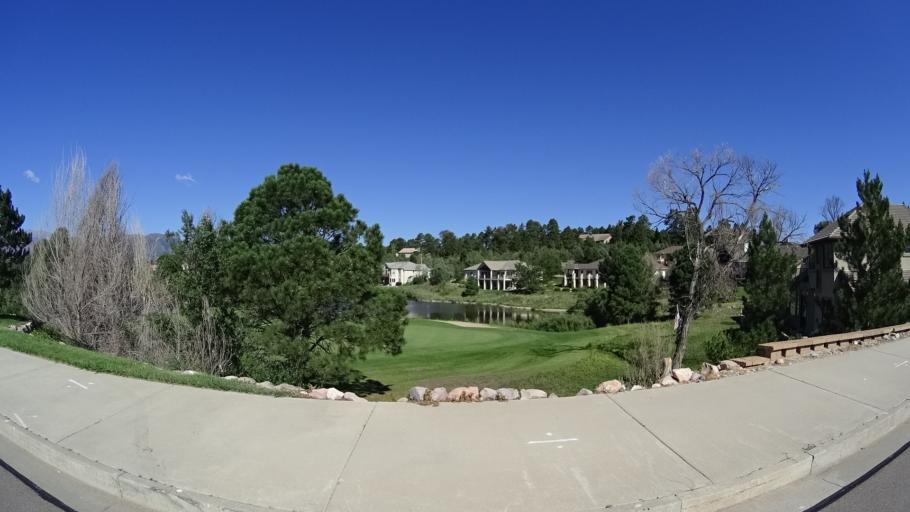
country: US
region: Colorado
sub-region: El Paso County
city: Air Force Academy
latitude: 38.9712
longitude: -104.7852
